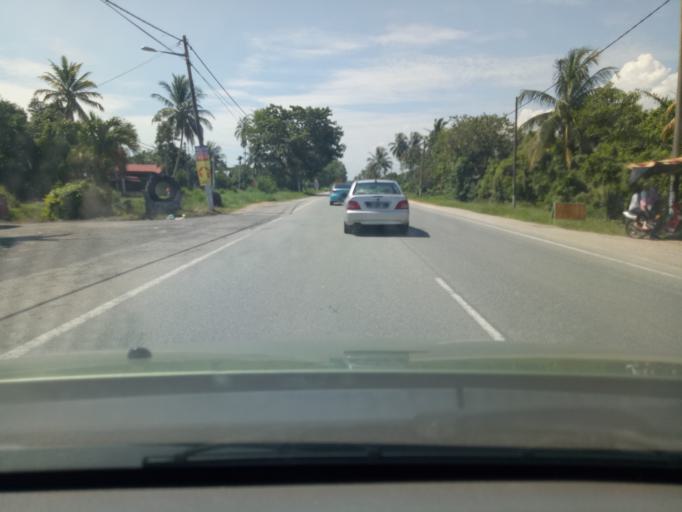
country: MY
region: Kedah
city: Gurun
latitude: 5.9467
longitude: 100.4103
